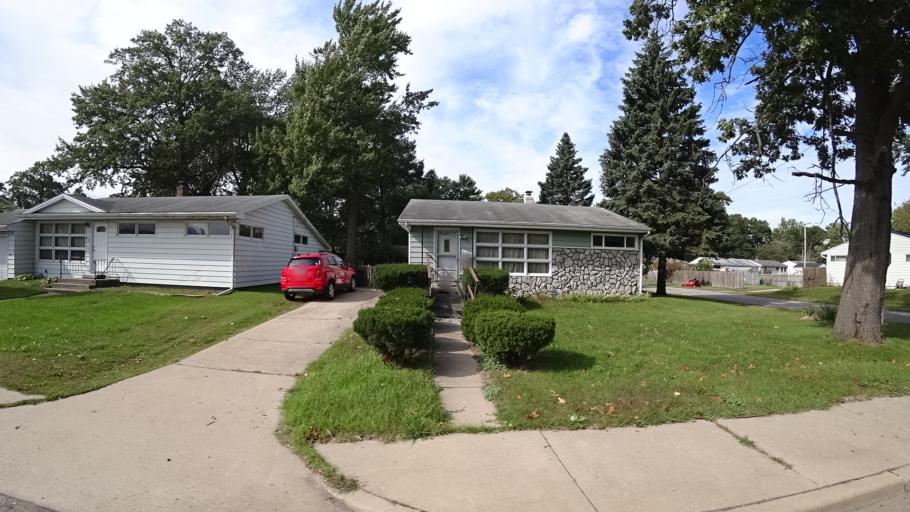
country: US
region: Indiana
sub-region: LaPorte County
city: Trail Creek
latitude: 41.7154
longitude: -86.8649
